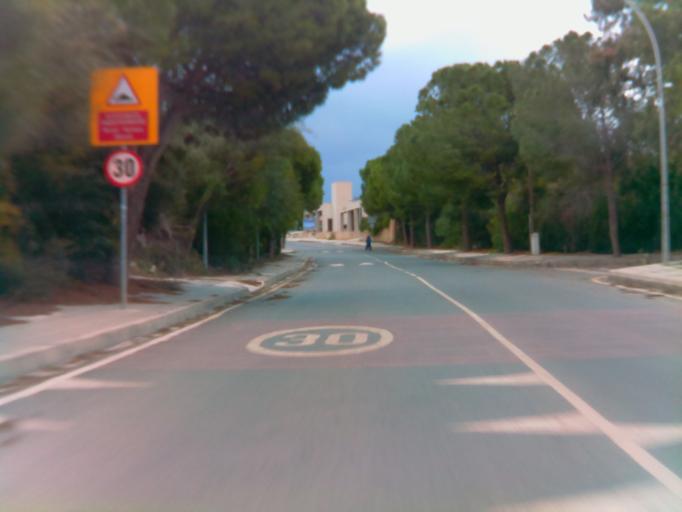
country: CY
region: Pafos
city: Pegeia
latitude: 34.8540
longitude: 32.3727
